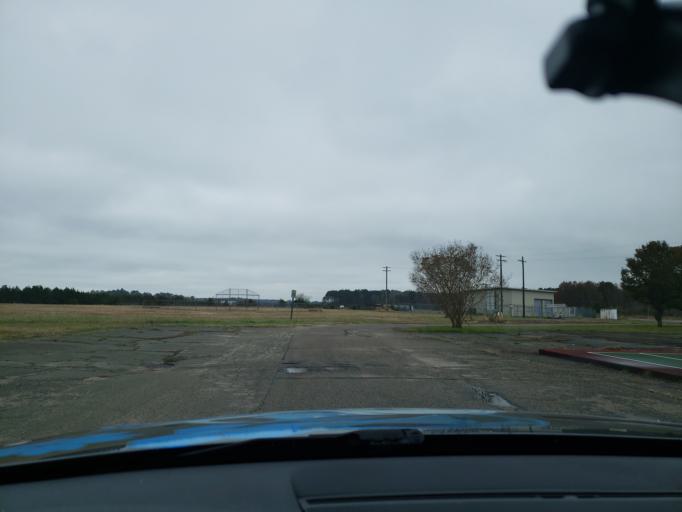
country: US
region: Virginia
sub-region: City of Chesapeake
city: Chesapeake
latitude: 36.7055
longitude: -76.1275
